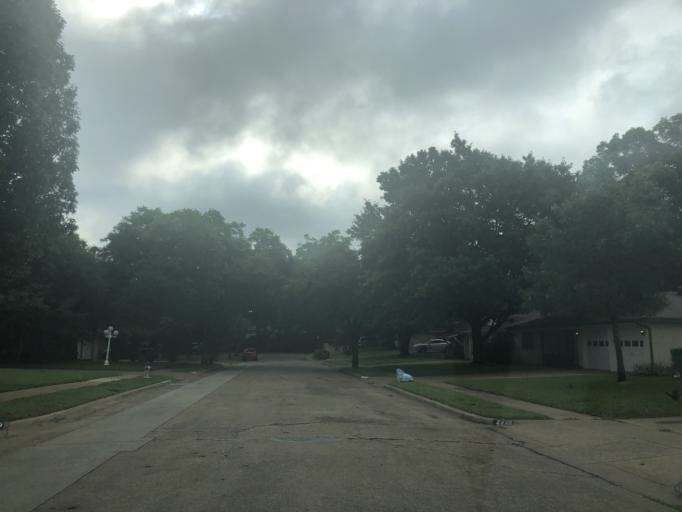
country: US
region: Texas
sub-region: Dallas County
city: Irving
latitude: 32.8056
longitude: -96.9761
